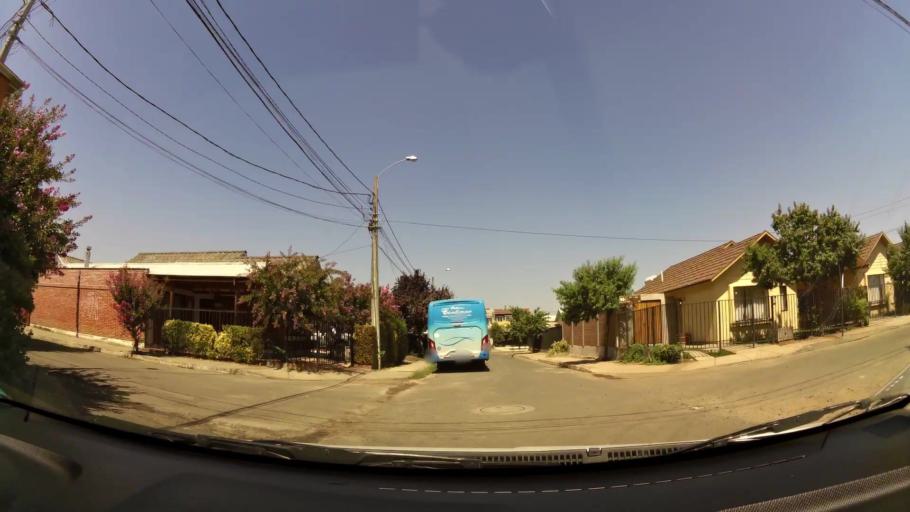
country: CL
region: Maule
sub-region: Provincia de Talca
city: Talca
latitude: -35.4223
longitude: -71.6290
